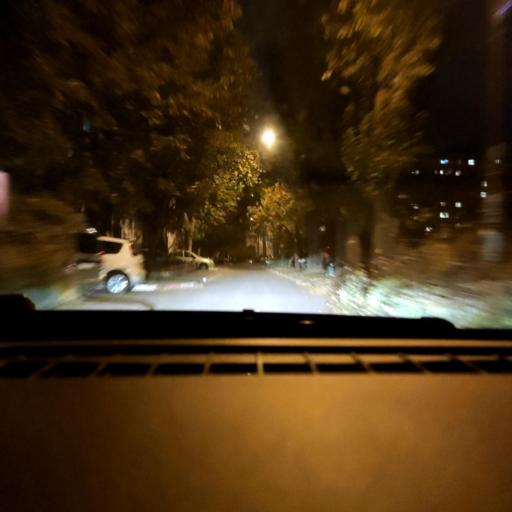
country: RU
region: Voronezj
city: Voronezh
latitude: 51.6729
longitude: 39.2467
